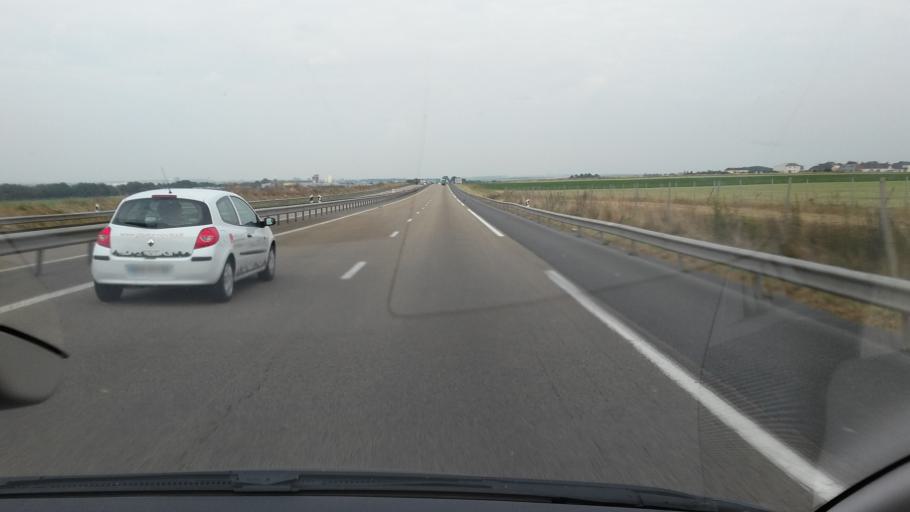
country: FR
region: Champagne-Ardenne
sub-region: Departement de la Marne
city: Witry-les-Reims
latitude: 49.3039
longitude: 4.1375
